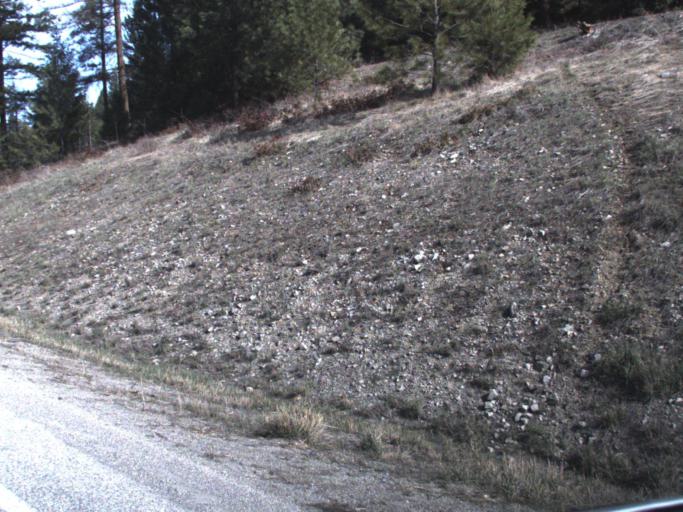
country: US
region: Washington
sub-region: Stevens County
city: Colville
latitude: 48.5253
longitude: -117.8177
